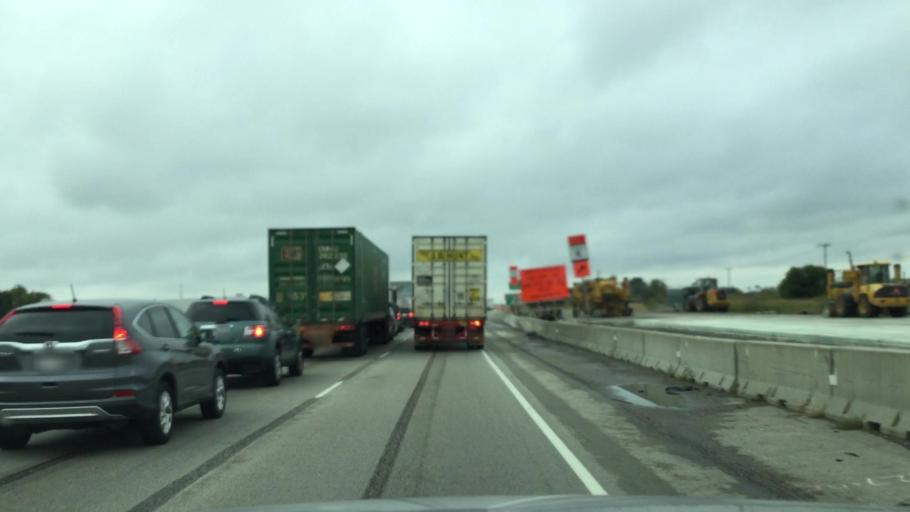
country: US
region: Wisconsin
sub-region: Racine County
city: Franksville
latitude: 42.7159
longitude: -87.9539
